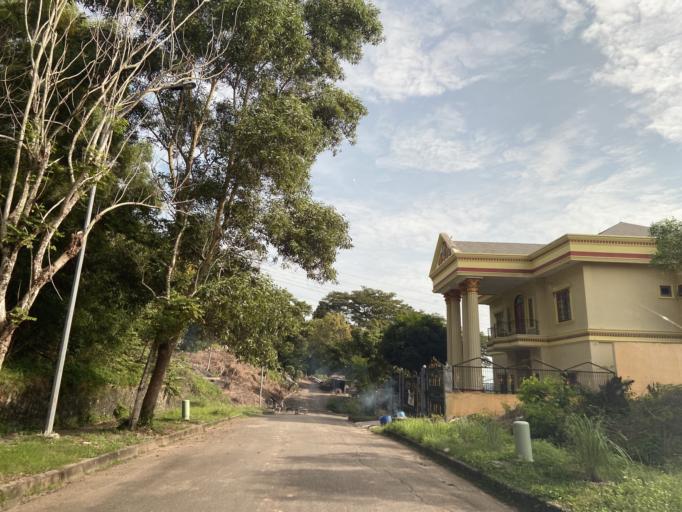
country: SG
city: Singapore
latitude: 1.1115
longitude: 104.0204
